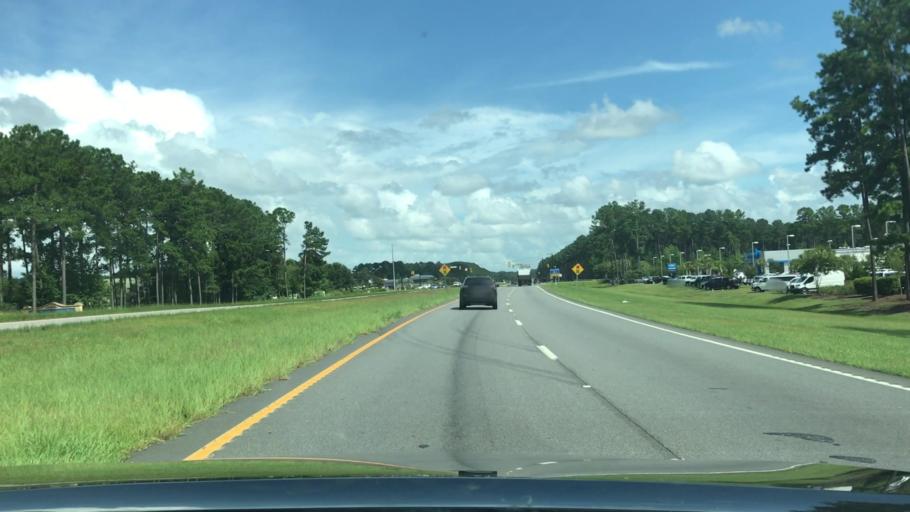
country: US
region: South Carolina
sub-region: Jasper County
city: Hardeeville
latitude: 32.3096
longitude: -80.9792
